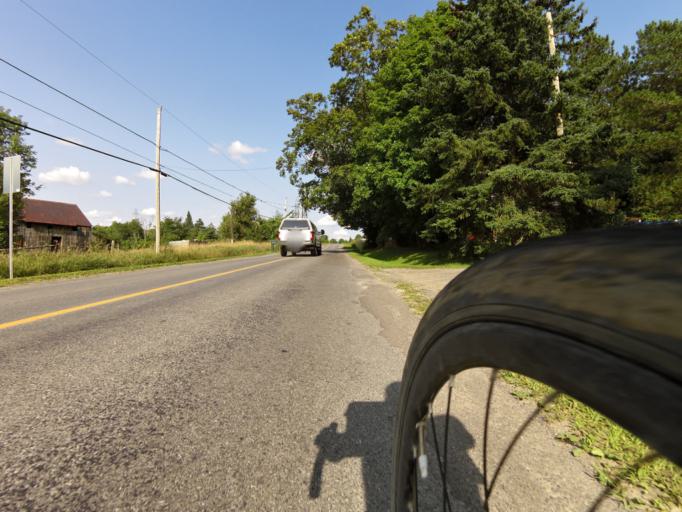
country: CA
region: Ontario
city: Kingston
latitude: 44.3641
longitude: -76.6280
